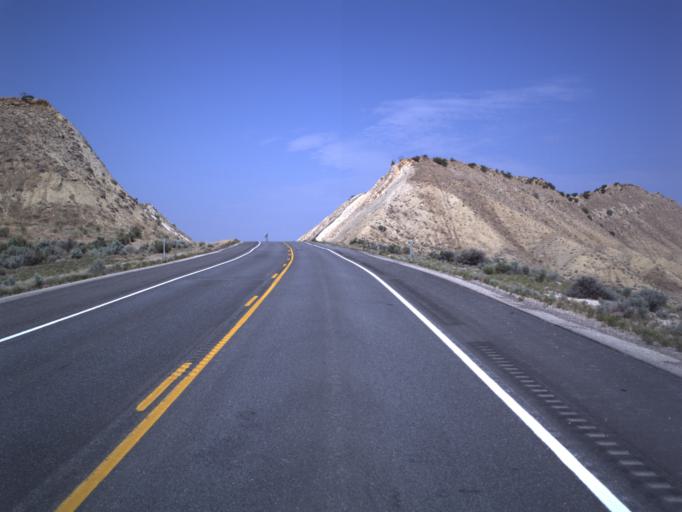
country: US
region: Colorado
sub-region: Rio Blanco County
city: Rangely
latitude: 40.2789
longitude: -109.0615
